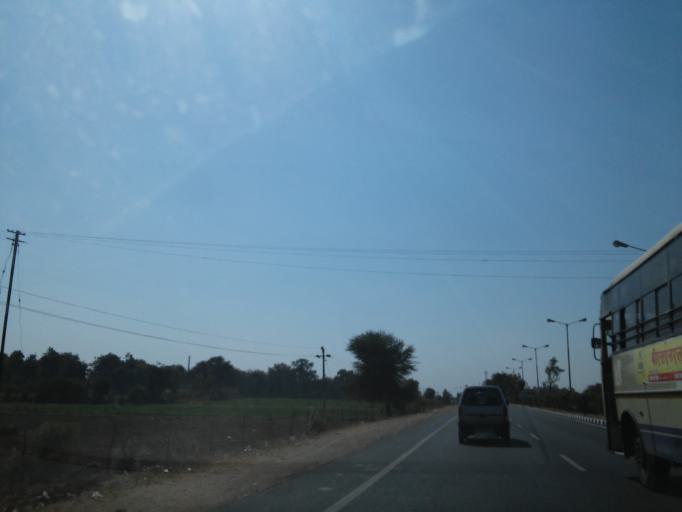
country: IN
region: Gujarat
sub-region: Gandhinagar
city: Chhala
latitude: 23.4054
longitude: 72.8250
